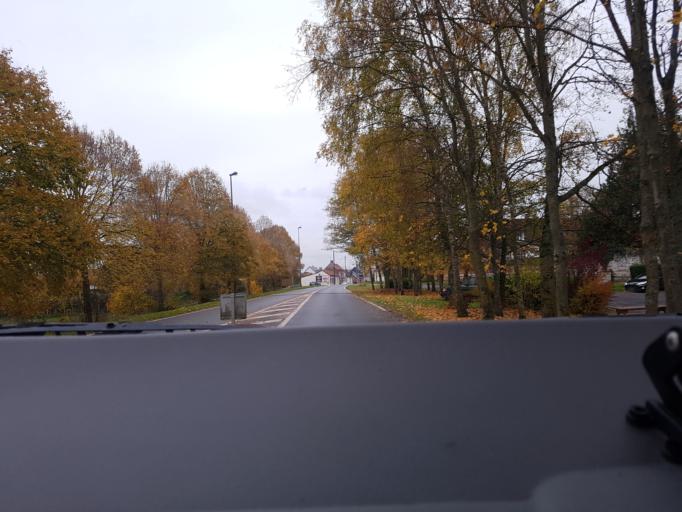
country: FR
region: Picardie
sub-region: Departement de la Somme
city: Abbeville
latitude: 50.1071
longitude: 1.7908
